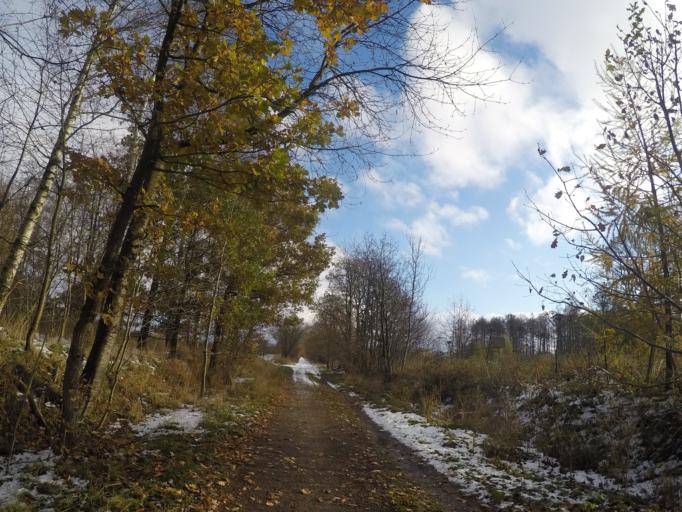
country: SE
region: Skane
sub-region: Lunds Kommun
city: Lund
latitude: 55.7840
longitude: 13.2261
